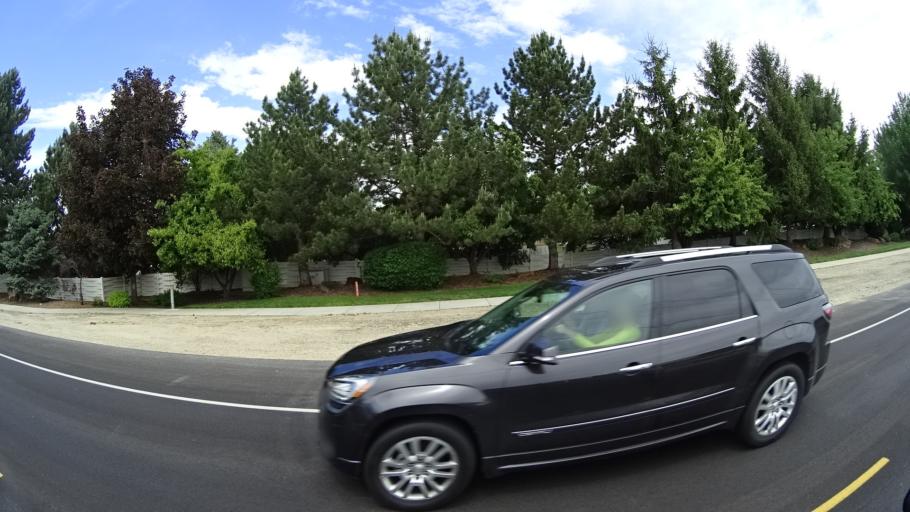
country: US
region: Idaho
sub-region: Ada County
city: Meridian
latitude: 43.5757
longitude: -116.3690
